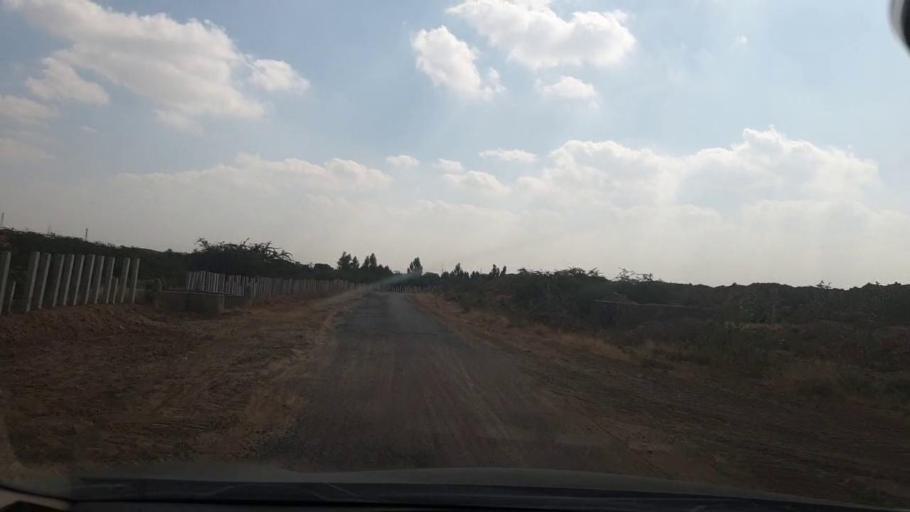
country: PK
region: Sindh
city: Malir Cantonment
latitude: 25.0234
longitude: 67.3537
